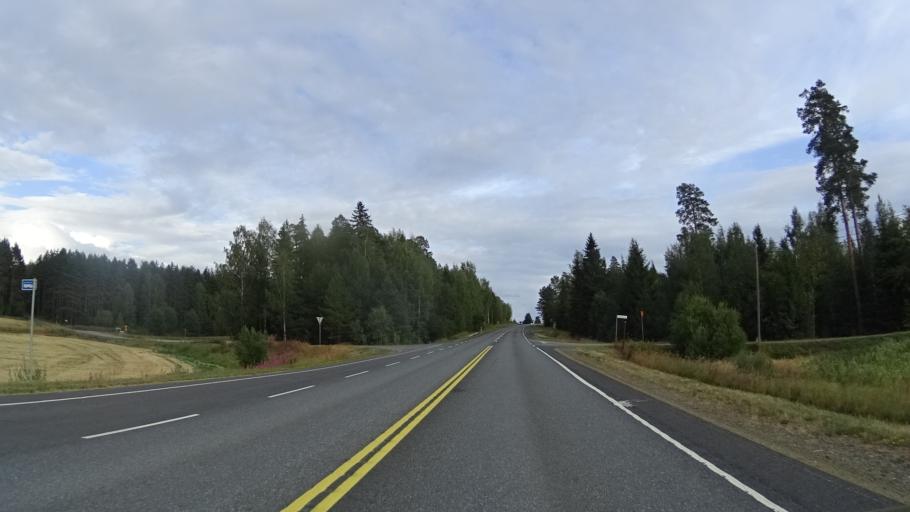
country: FI
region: Haeme
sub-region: Haemeenlinna
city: Parola
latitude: 61.0358
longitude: 24.2643
